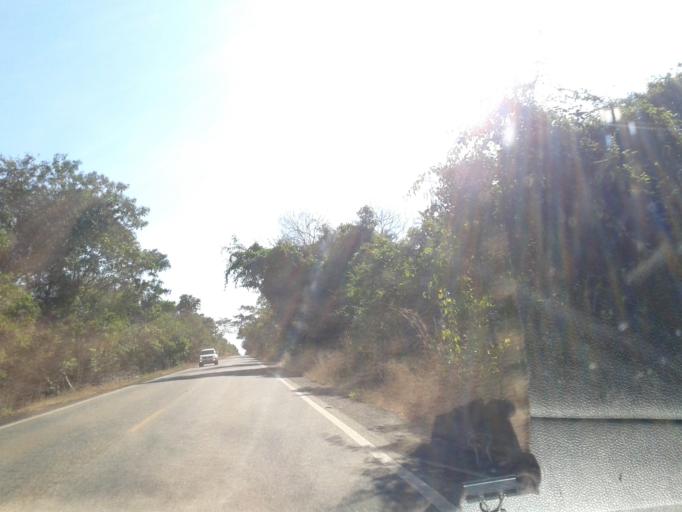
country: BR
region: Goias
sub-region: Mozarlandia
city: Mozarlandia
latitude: -14.6038
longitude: -50.5127
